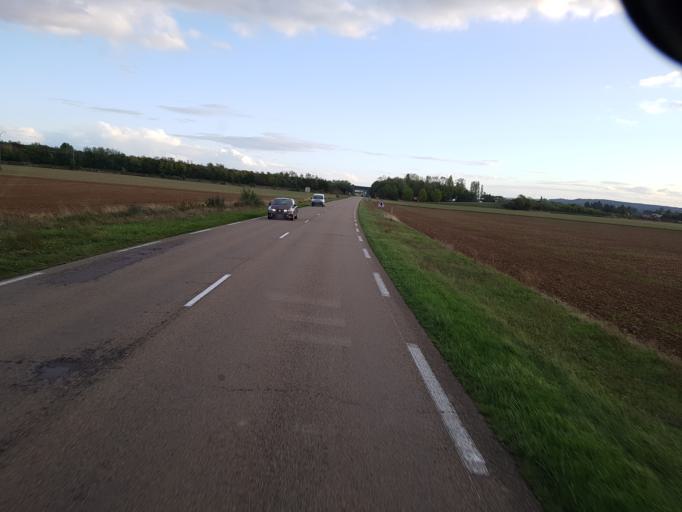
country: FR
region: Bourgogne
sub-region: Departement de l'Yonne
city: Soucy
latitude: 48.2612
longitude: 3.2828
